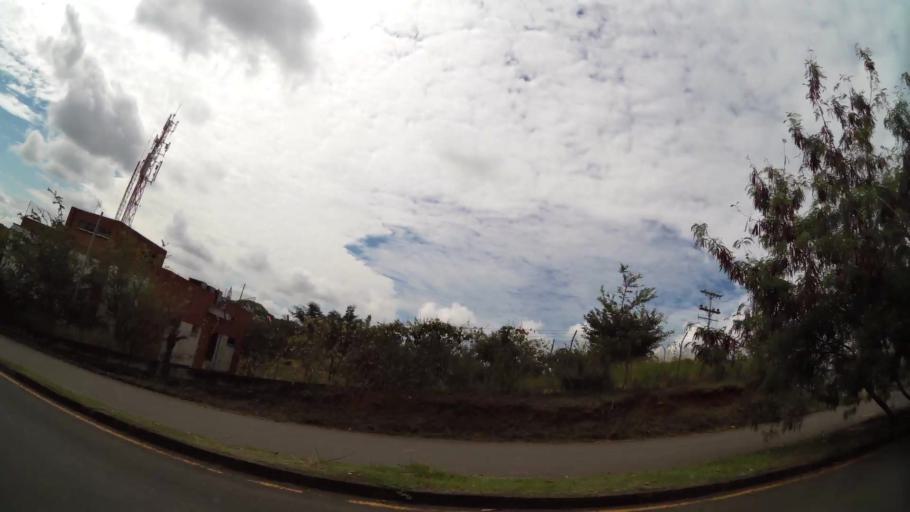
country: CO
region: Valle del Cauca
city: Cali
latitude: 3.3860
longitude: -76.5513
